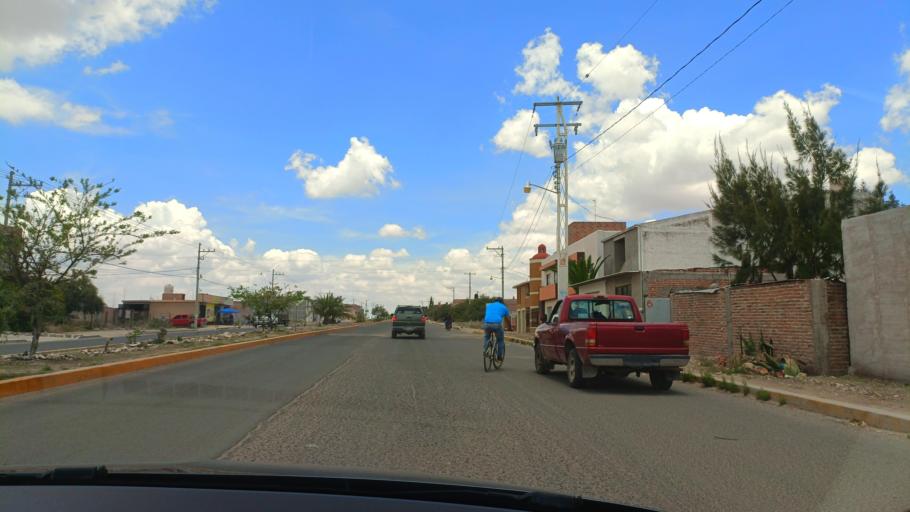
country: MX
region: Guanajuato
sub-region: San Luis de la Paz
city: San Luis de la Paz
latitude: 21.2899
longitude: -100.4929
